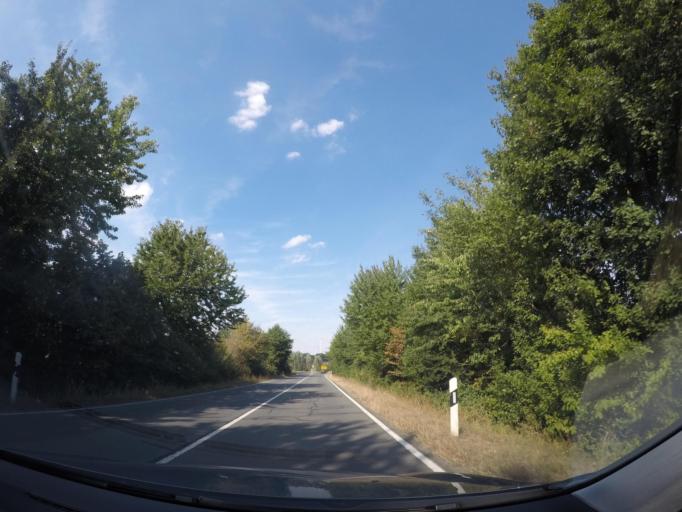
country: DE
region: Saxony-Anhalt
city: Heudeber
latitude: 51.9687
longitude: 10.8336
